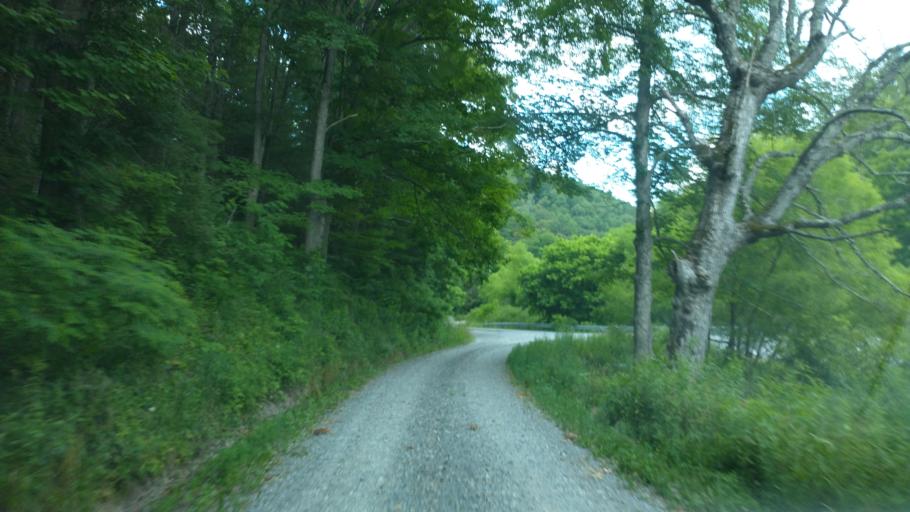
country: US
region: West Virginia
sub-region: Mercer County
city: Athens
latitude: 37.4273
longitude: -80.9952
